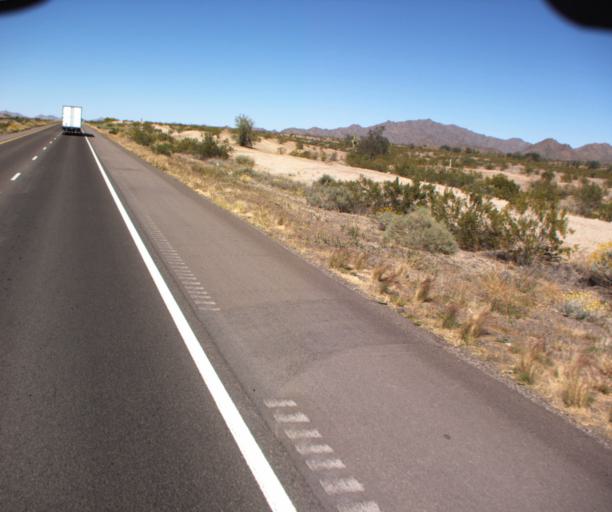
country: US
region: Arizona
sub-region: Maricopa County
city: Gila Bend
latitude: 33.0875
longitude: -112.6478
